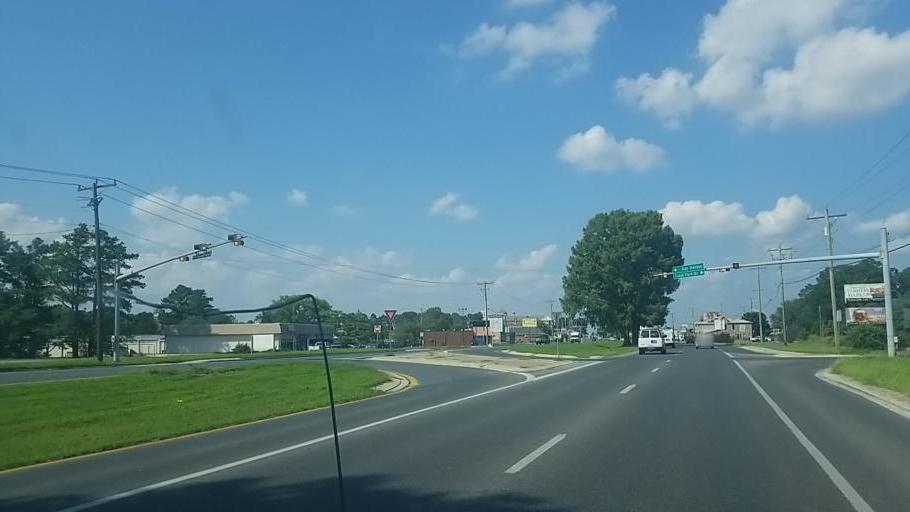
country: US
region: Maryland
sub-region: Wicomico County
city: Fruitland
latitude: 38.3365
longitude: -75.6081
